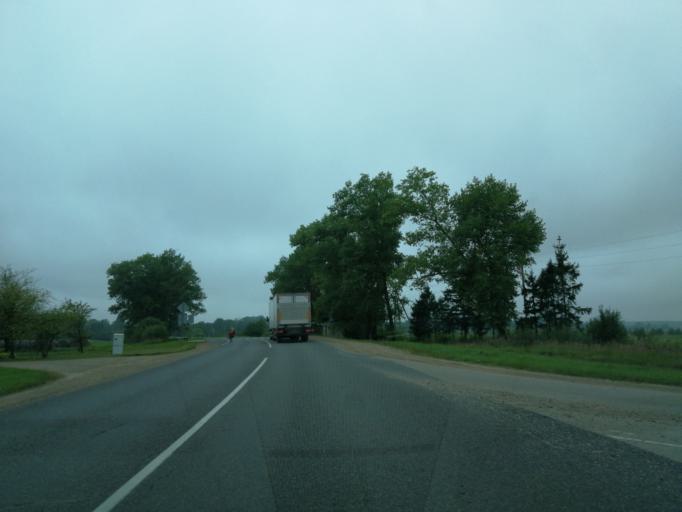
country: LV
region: Livani
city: Livani
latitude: 56.3416
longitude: 26.3550
